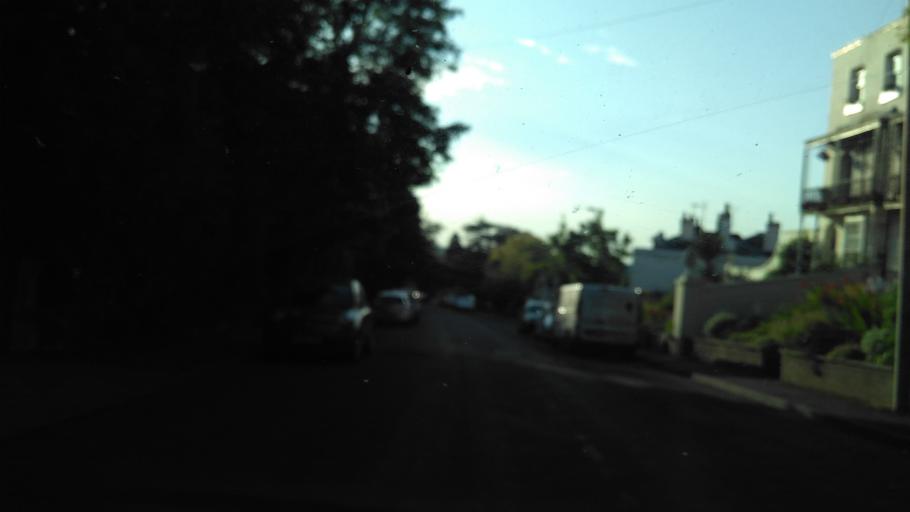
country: GB
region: England
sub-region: Kent
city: Canterbury
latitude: 51.2818
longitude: 1.0575
